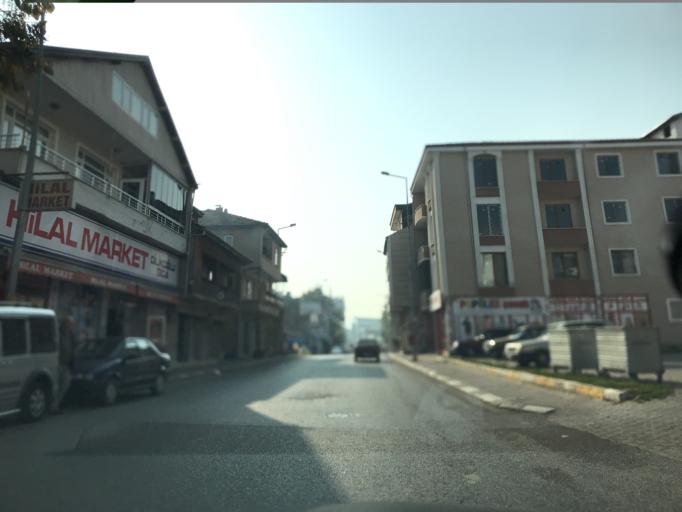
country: TR
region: Duzce
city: Cumayeri
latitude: 40.8764
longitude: 30.9501
